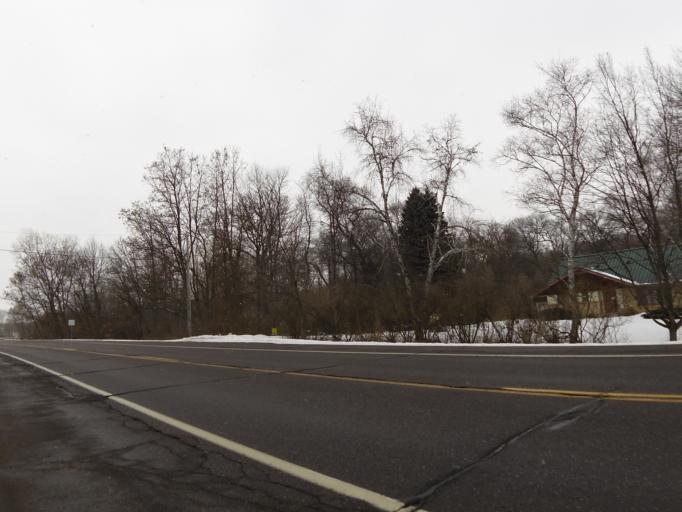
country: US
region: Minnesota
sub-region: Washington County
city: Lake Elmo
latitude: 44.9648
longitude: -92.8414
